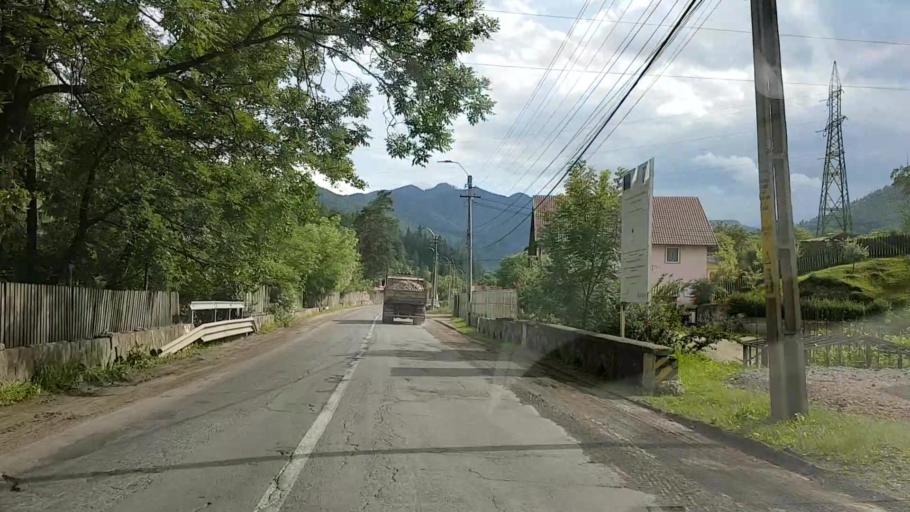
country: RO
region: Neamt
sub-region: Comuna Bicaz
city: Dodeni
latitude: 46.9291
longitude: 26.0952
